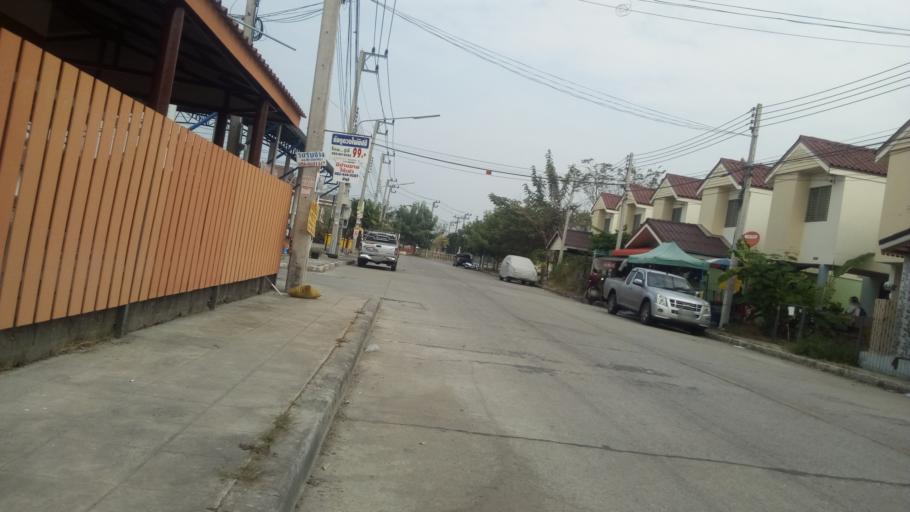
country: TH
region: Pathum Thani
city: Nong Suea
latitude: 14.0555
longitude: 100.8415
